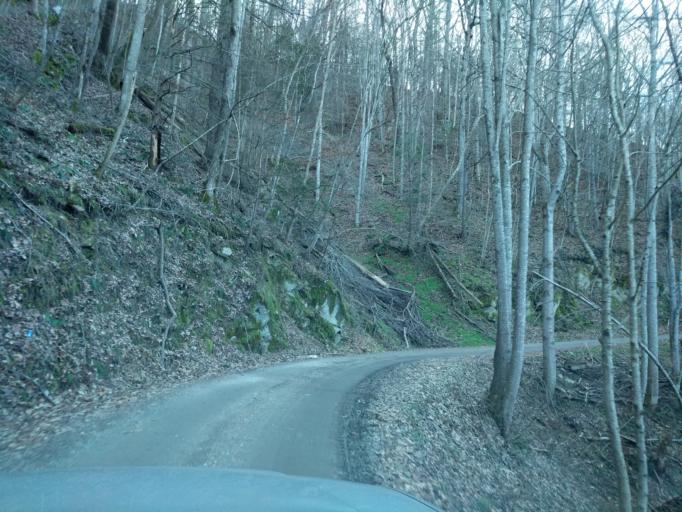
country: US
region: North Carolina
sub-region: Haywood County
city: Cove Creek
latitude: 35.7320
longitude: -83.0268
